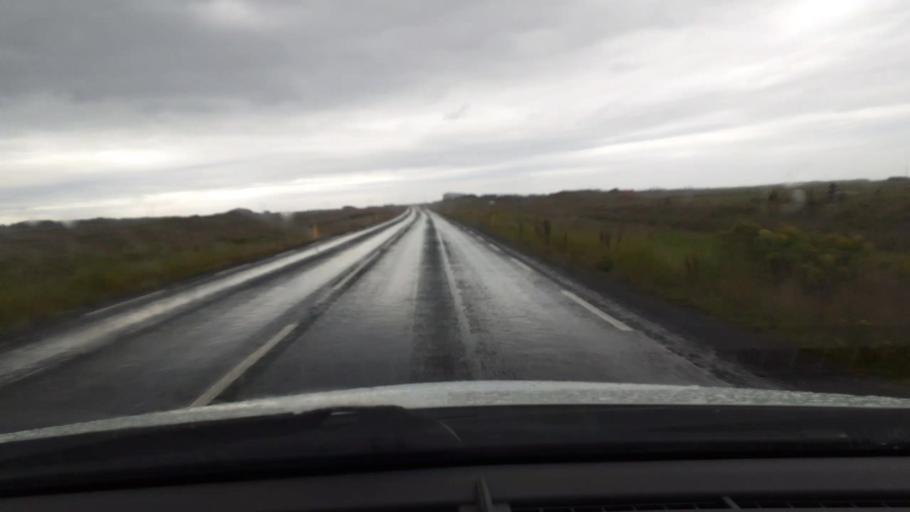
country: IS
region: West
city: Akranes
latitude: 64.3386
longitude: -22.0237
